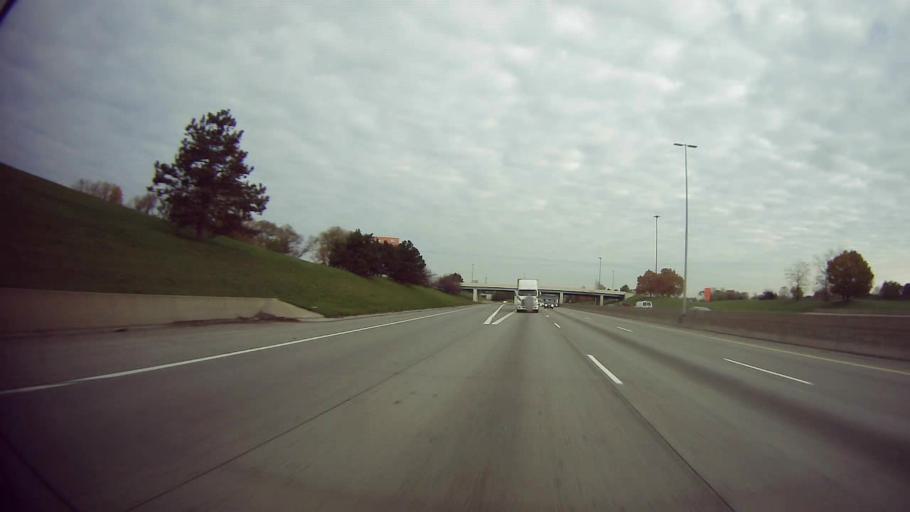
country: US
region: Michigan
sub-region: Wayne County
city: Dearborn
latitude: 42.3233
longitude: -83.1635
